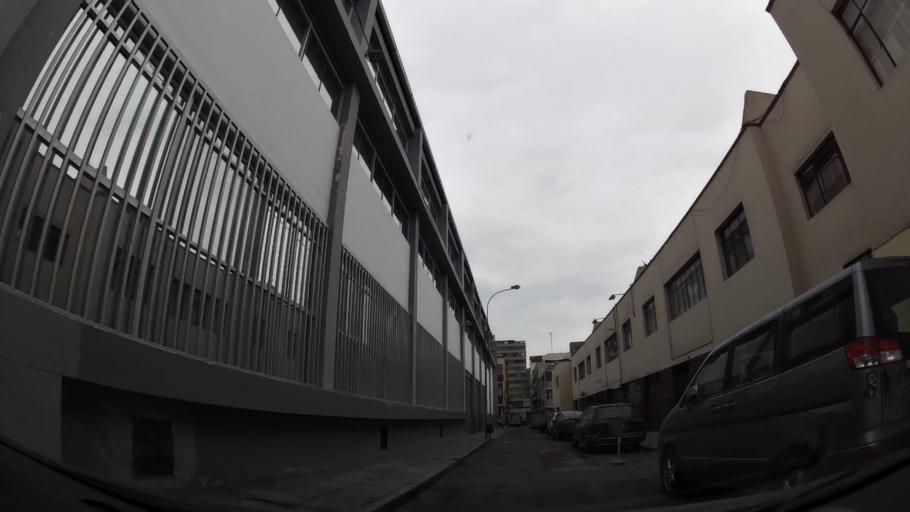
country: PE
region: Lima
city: Lima
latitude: -12.0615
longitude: -77.0396
